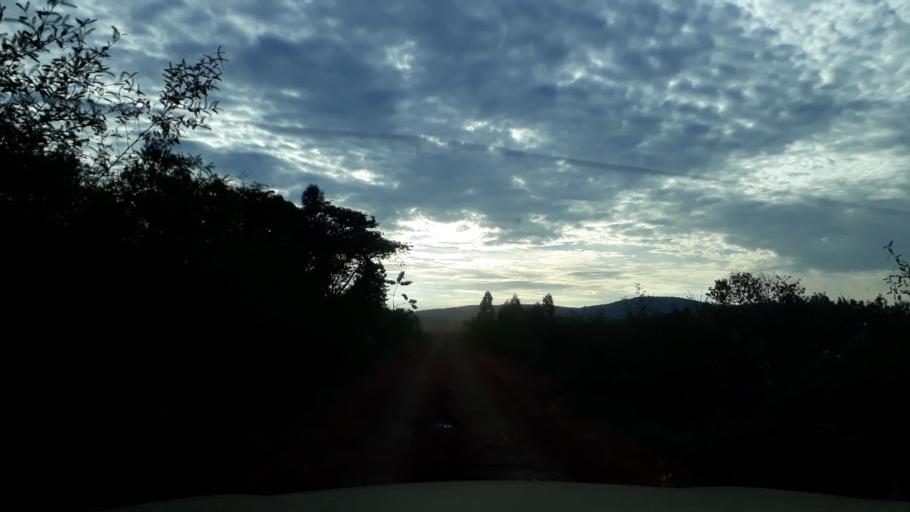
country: UG
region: Northern Region
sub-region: Zombo District
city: Paidha
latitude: 2.2228
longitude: 30.8023
